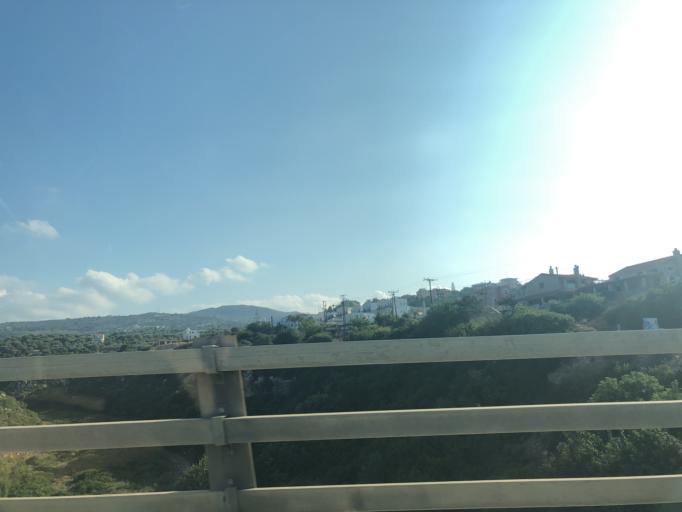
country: GR
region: Crete
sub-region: Nomos Rethymnis
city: Atsipopoulon
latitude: 35.3592
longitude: 24.4062
